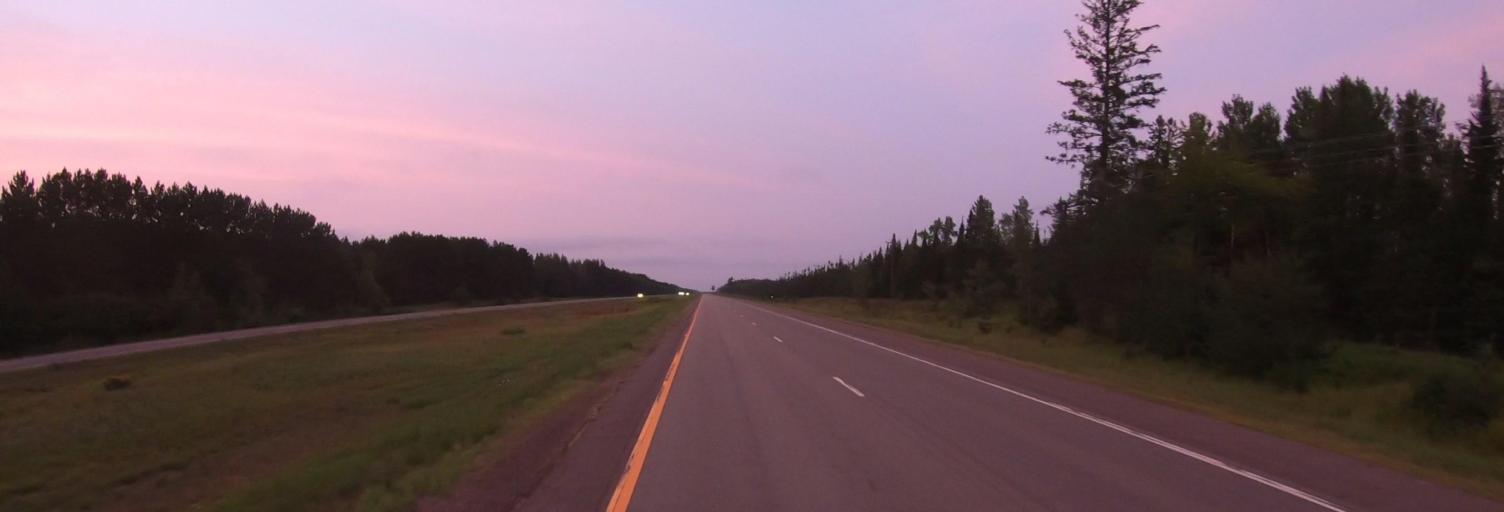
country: US
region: Minnesota
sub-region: Saint Louis County
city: Hermantown
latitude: 47.0906
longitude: -92.4715
